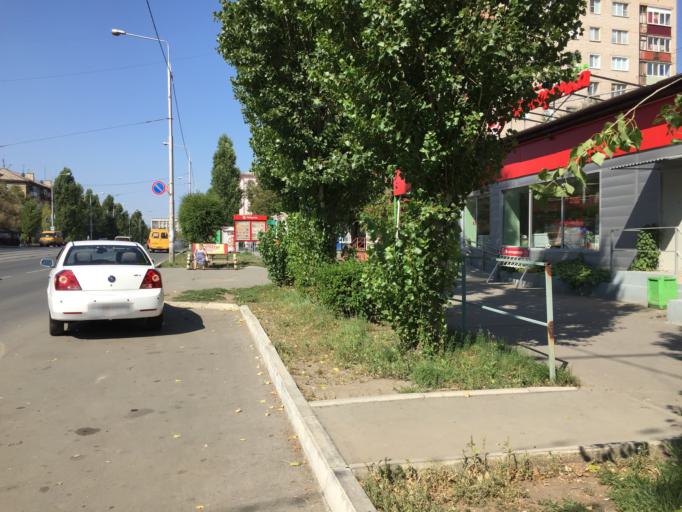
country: RU
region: Orenburg
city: Novotroitsk
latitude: 51.1963
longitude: 58.3060
